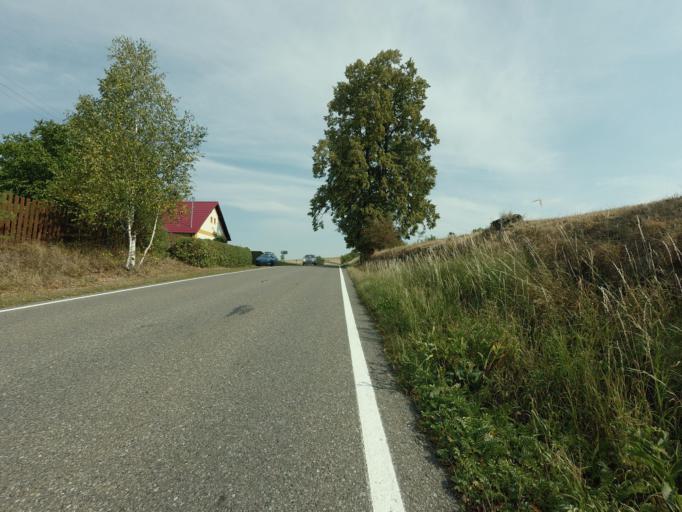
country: CZ
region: Jihocesky
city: Milevsko
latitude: 49.5040
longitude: 14.3635
